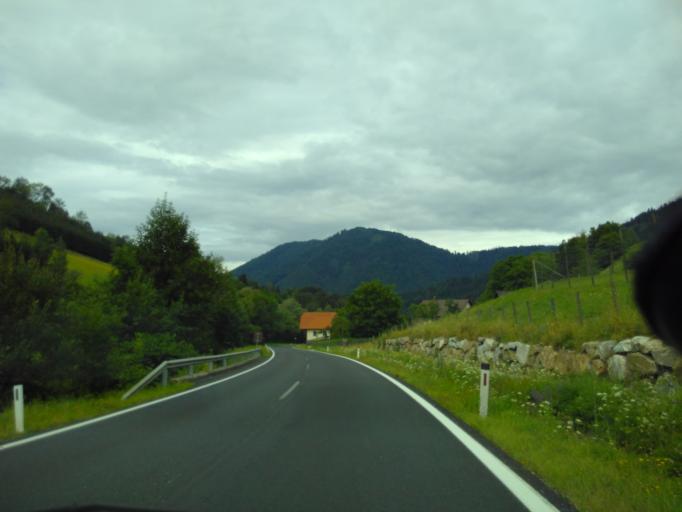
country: AT
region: Styria
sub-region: Politischer Bezirk Graz-Umgebung
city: Schrems bei Frohnleiten
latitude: 47.2759
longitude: 15.3821
